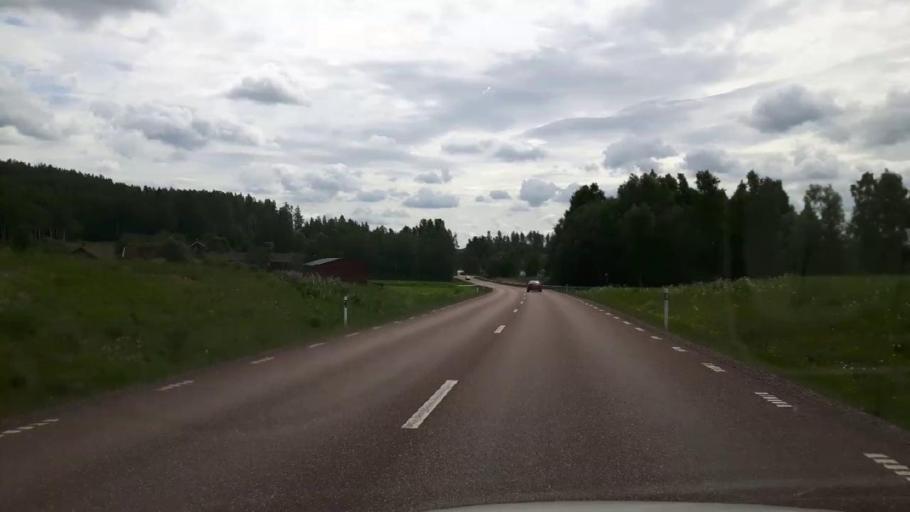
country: SE
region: Dalarna
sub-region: Hedemora Kommun
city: Hedemora
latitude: 60.3267
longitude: 15.9506
